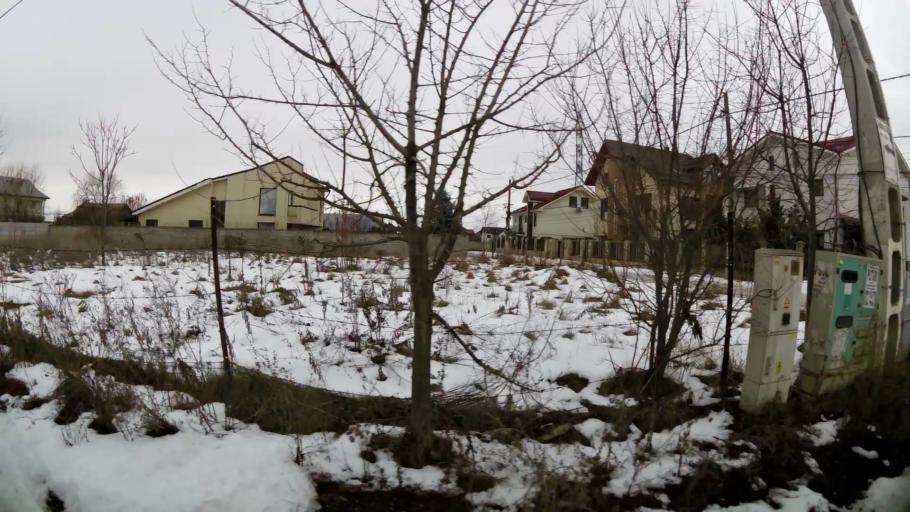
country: RO
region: Ilfov
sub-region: Comuna Pantelimon
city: Pantelimon
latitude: 44.4555
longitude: 26.2206
